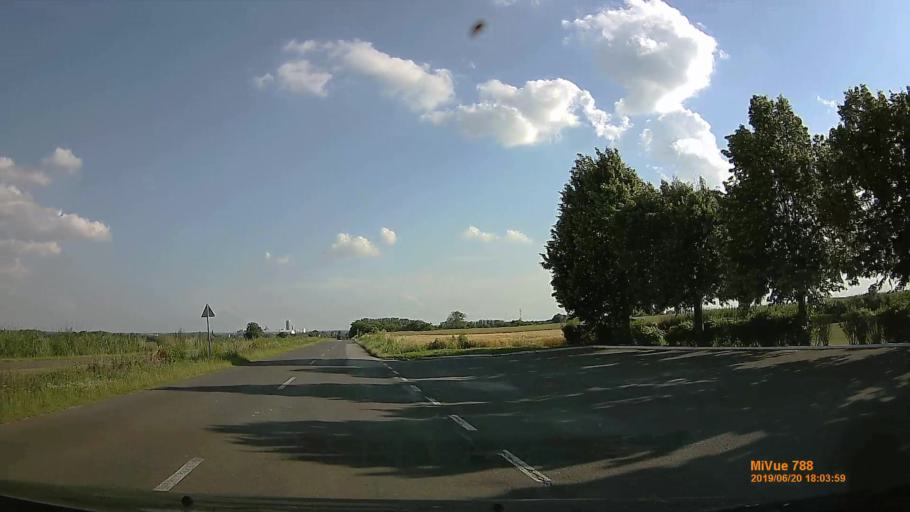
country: HU
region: Baranya
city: Szentlorinc
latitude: 46.0557
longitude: 17.9898
